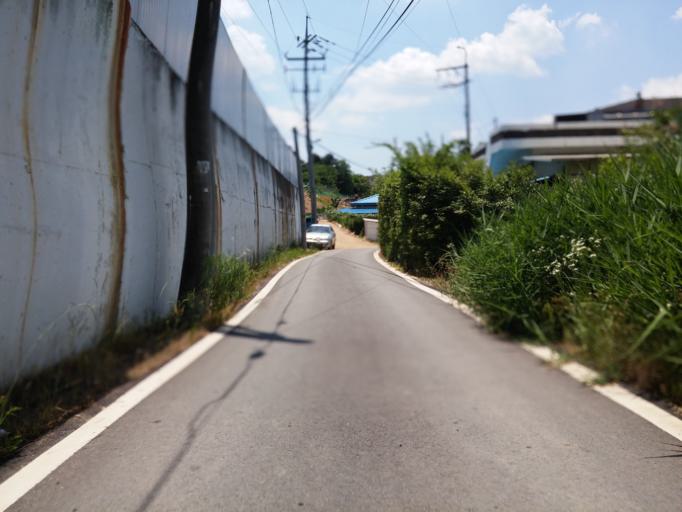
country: KR
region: Chungcheongbuk-do
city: Cheongju-si
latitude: 36.5608
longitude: 127.4391
